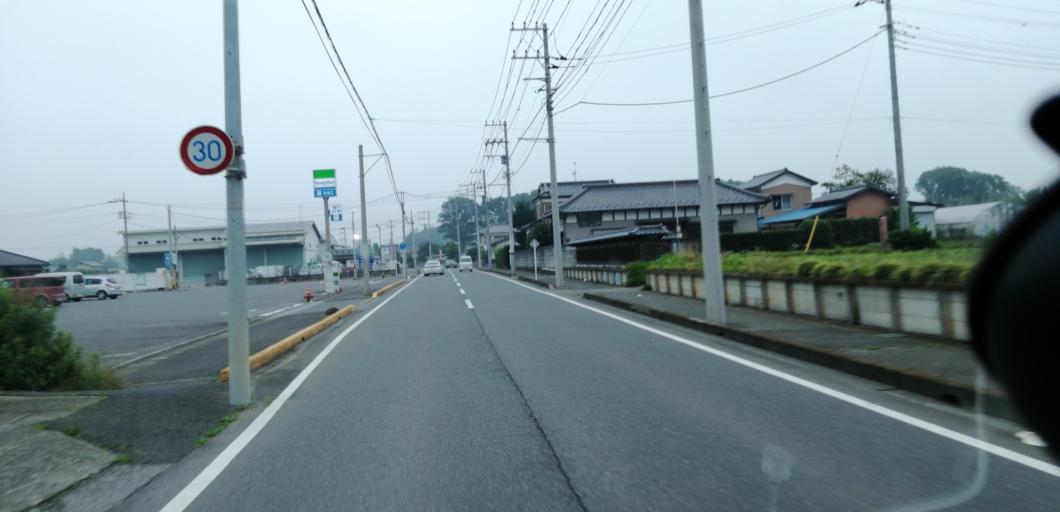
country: JP
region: Ibaraki
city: Iwai
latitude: 36.0156
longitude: 139.8470
